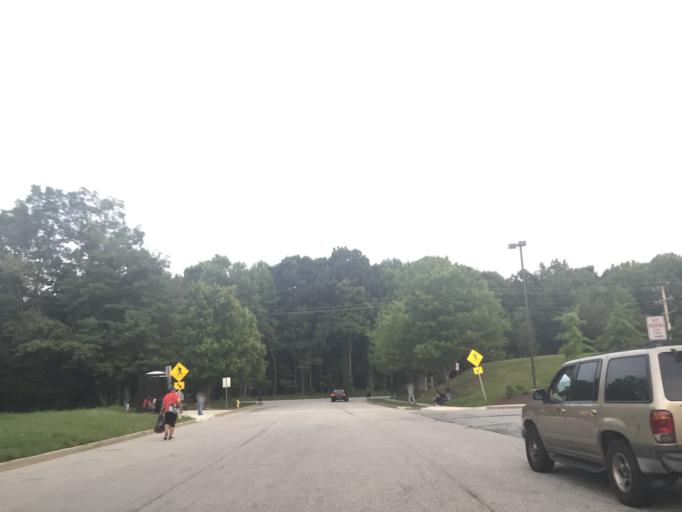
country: US
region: Maryland
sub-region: Anne Arundel County
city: Riviera Beach
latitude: 39.1931
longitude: -76.5516
